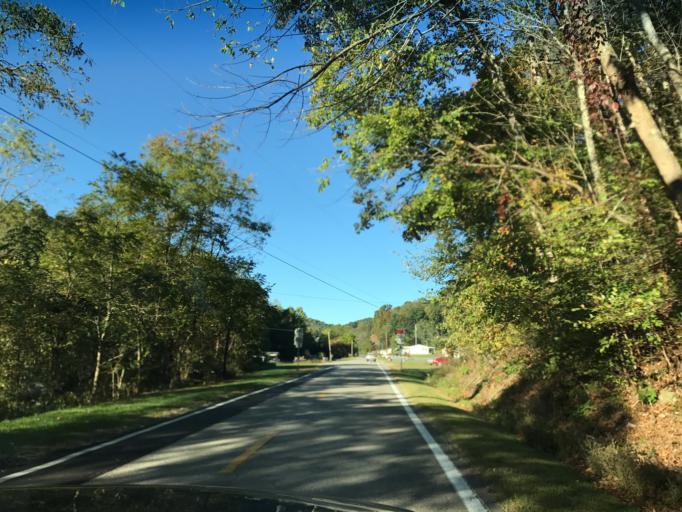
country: US
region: West Virginia
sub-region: Ritchie County
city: Harrisville
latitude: 39.3056
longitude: -81.1131
